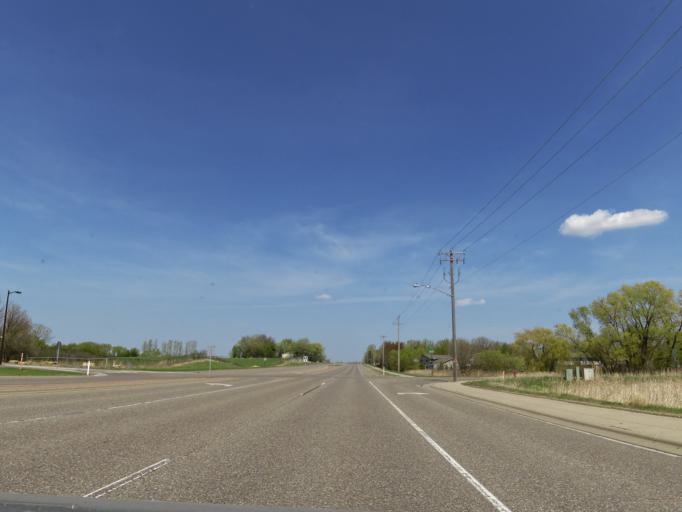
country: US
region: Minnesota
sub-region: Scott County
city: Savage
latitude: 44.7569
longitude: -93.3590
